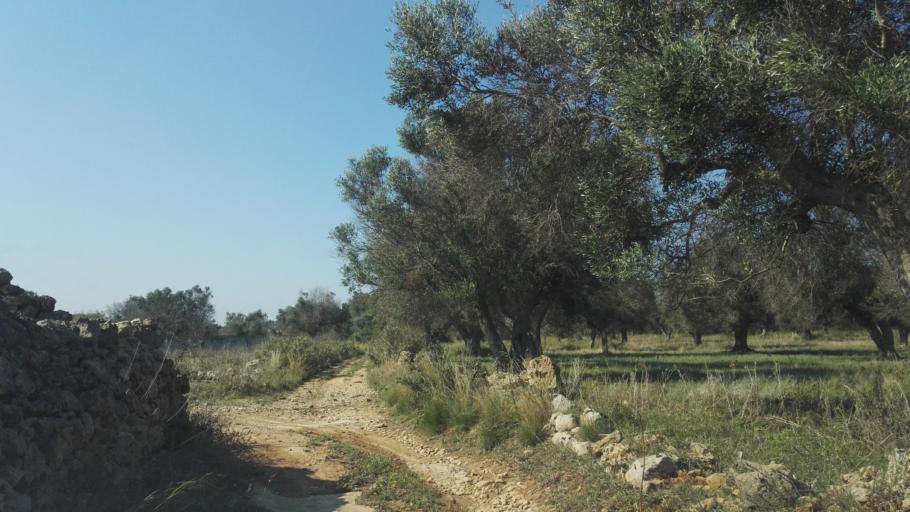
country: IT
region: Apulia
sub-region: Provincia di Lecce
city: Alezio
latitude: 40.0511
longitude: 18.0317
